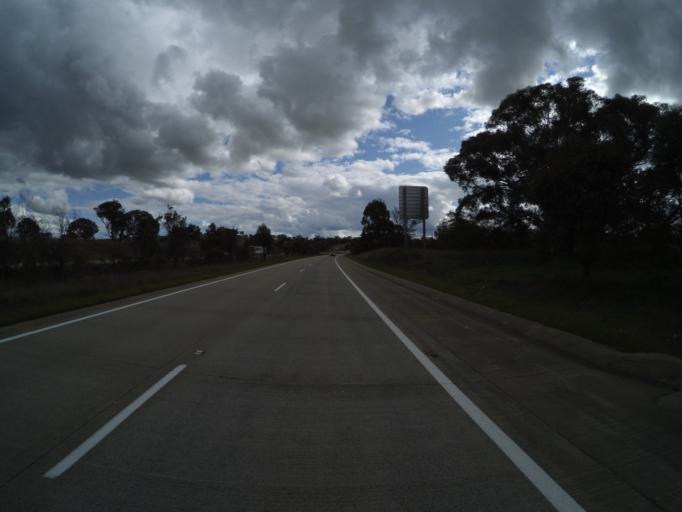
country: AU
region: New South Wales
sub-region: Yass Valley
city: Gundaroo
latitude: -34.7884
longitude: 149.2364
